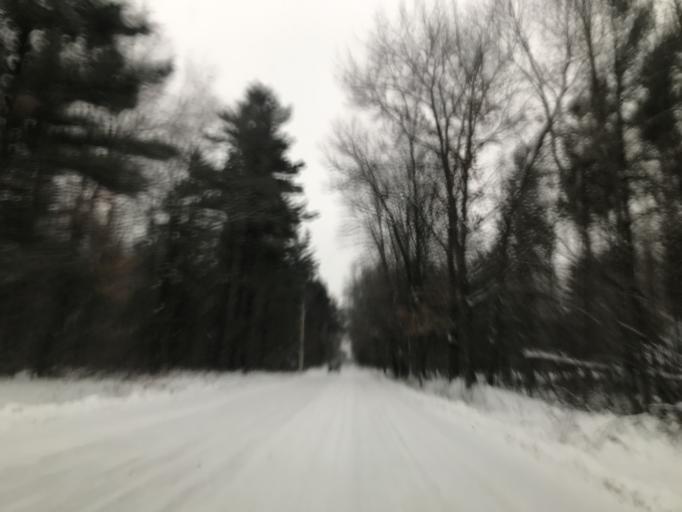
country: US
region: Wisconsin
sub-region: Marinette County
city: Peshtigo
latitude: 45.0460
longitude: -87.7195
